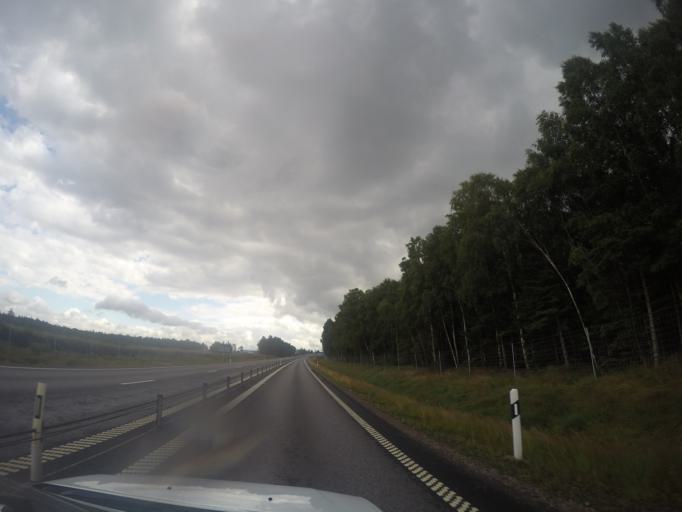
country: SE
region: Kronoberg
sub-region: Ljungby Kommun
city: Ljungby
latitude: 56.8103
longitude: 13.8937
